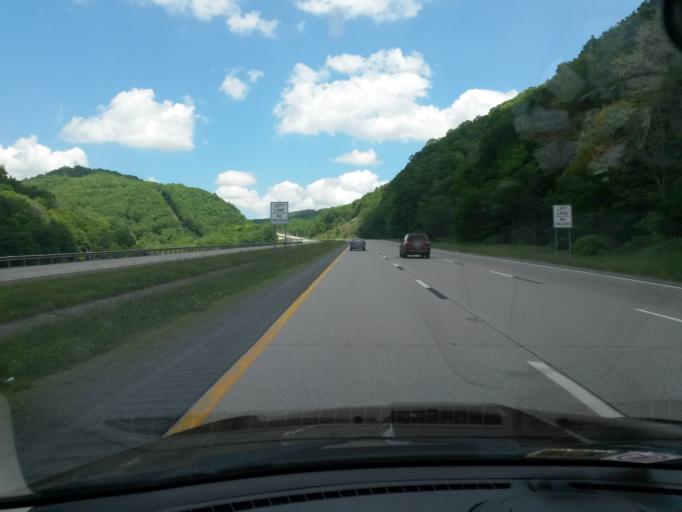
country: US
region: West Virginia
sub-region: Greenbrier County
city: Rainelle
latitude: 37.8303
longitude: -80.7876
